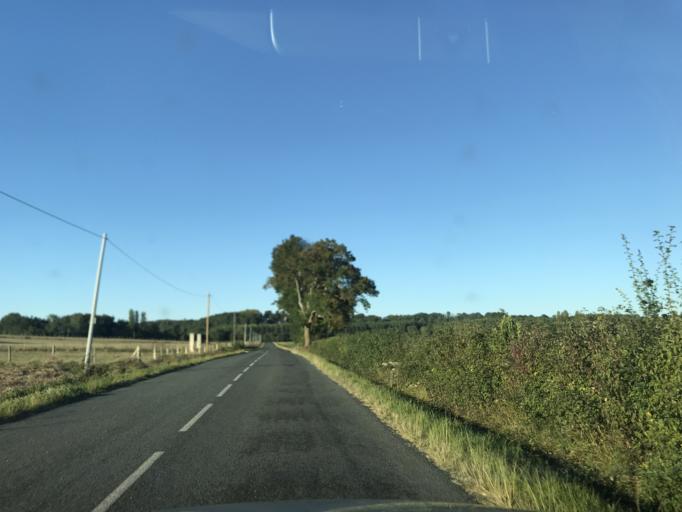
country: FR
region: Aquitaine
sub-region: Departement de la Gironde
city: Rauzan
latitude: 44.7669
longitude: -0.0642
